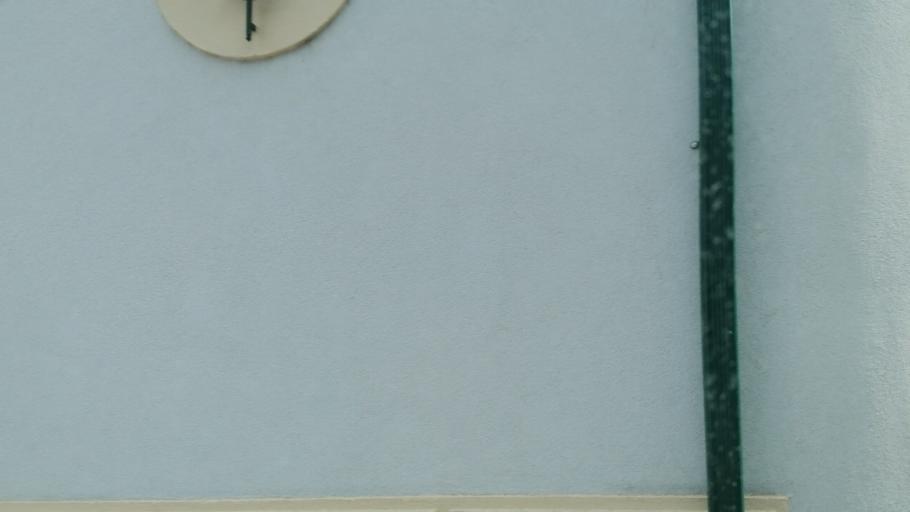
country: PT
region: Viseu
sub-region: Tabuaco
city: Tabuaco
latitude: 41.1705
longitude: -7.5392
